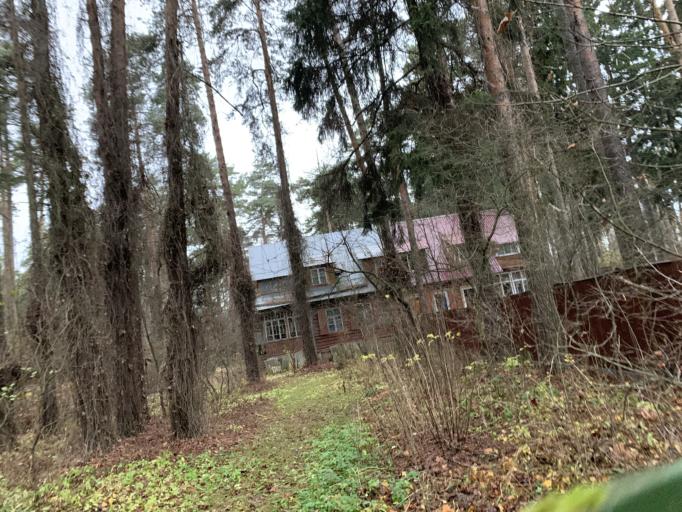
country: RU
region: Moskovskaya
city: Mamontovka
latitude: 55.9864
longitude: 37.8149
